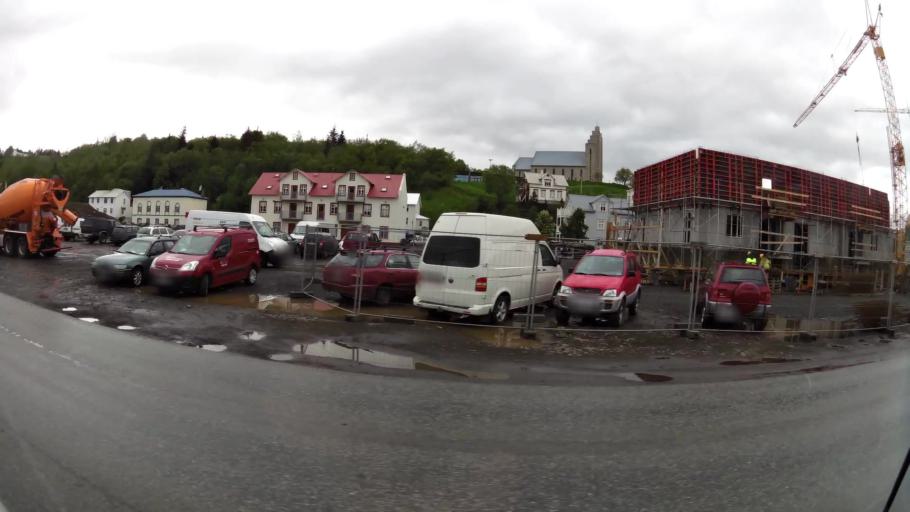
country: IS
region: Northeast
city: Akureyri
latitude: 65.6794
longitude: -18.0875
